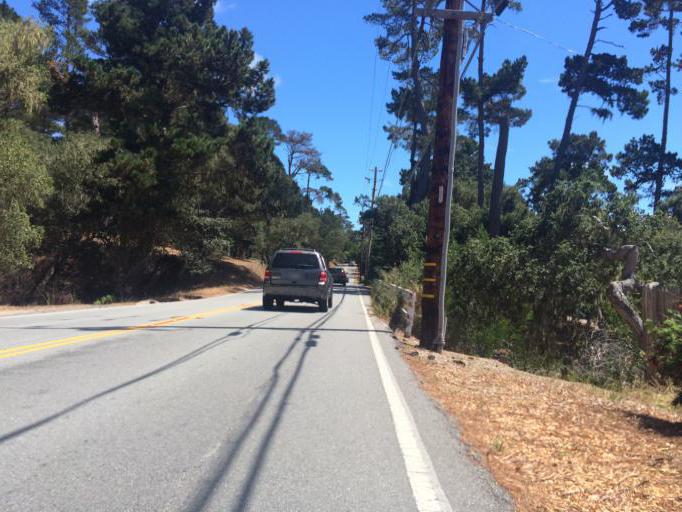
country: US
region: California
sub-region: Monterey County
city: Carmel-by-the-Sea
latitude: 36.5632
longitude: -121.9310
